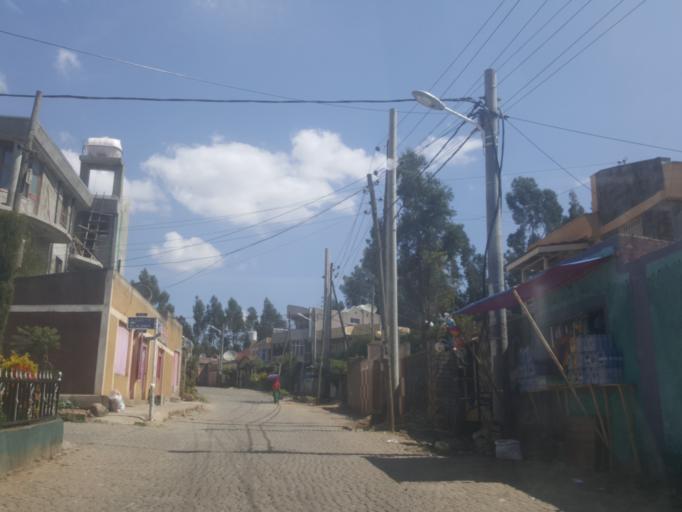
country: ET
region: Adis Abeba
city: Addis Ababa
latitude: 9.0665
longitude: 38.7192
